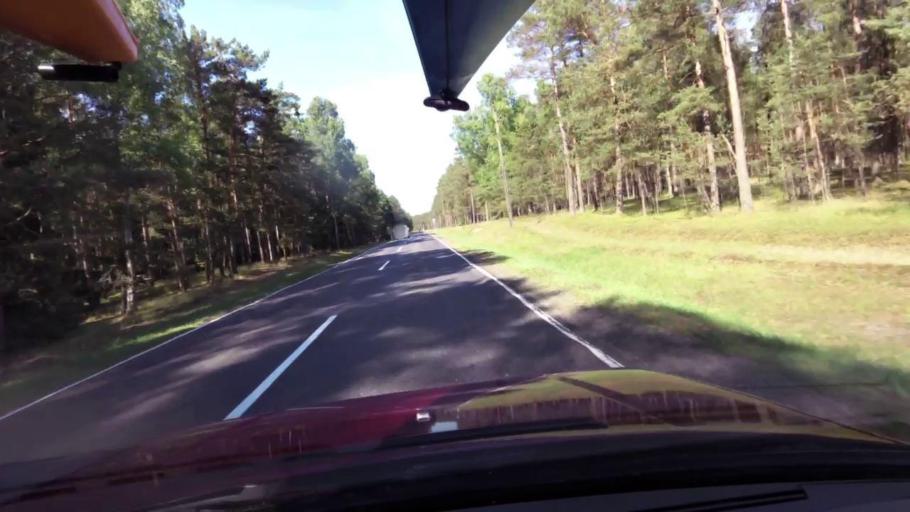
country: PL
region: Pomeranian Voivodeship
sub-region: Powiat bytowski
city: Trzebielino
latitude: 54.1617
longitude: 17.0538
